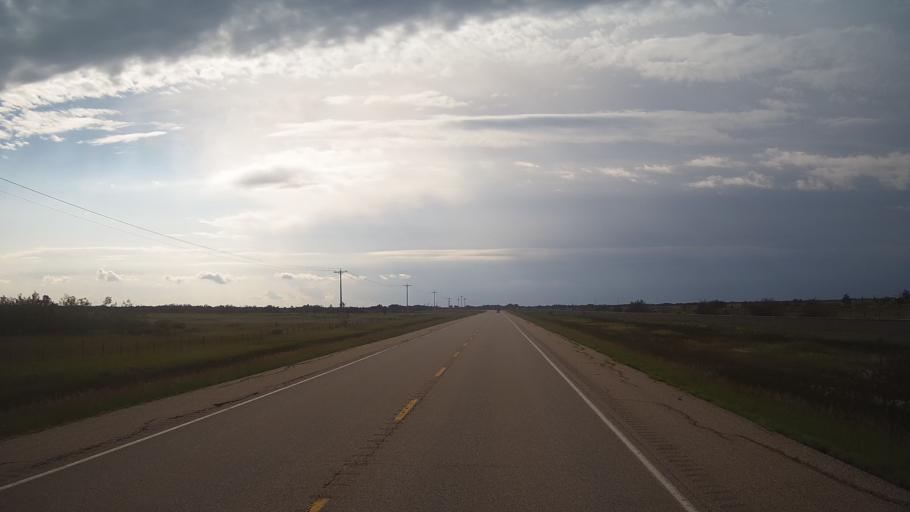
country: CA
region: Alberta
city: Viking
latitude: 53.1284
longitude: -111.8973
